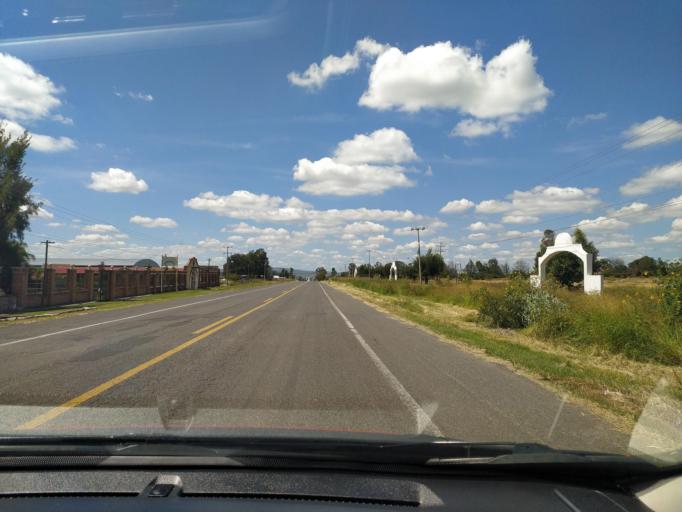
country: MX
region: Jalisco
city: San Miguel el Alto
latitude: 21.0193
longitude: -102.3439
